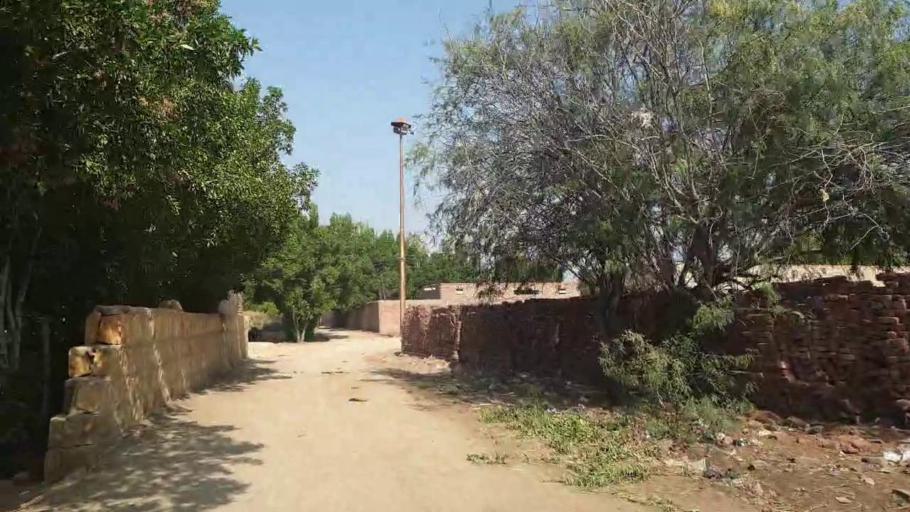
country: PK
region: Sindh
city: Jamshoro
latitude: 25.4804
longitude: 68.2844
